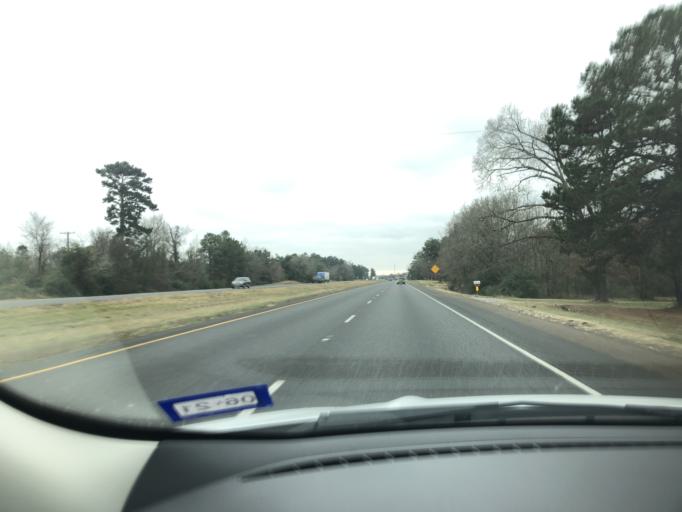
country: US
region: Texas
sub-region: Angelina County
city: Redland
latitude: 31.5000
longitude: -94.7094
